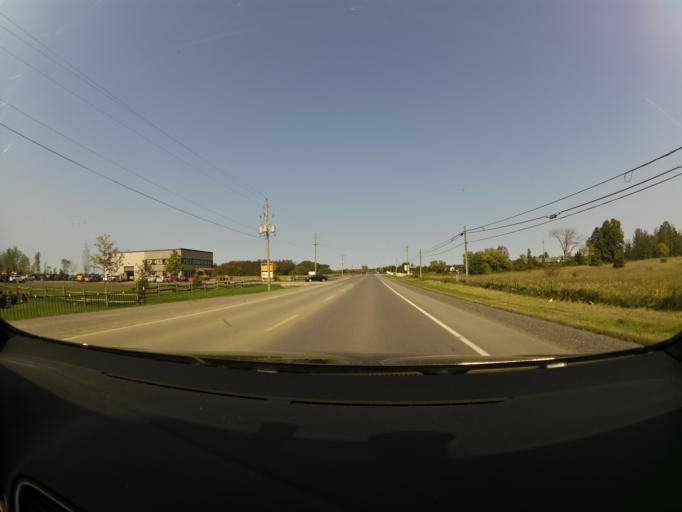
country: CA
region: Ontario
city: Bells Corners
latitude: 45.3203
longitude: -76.0057
